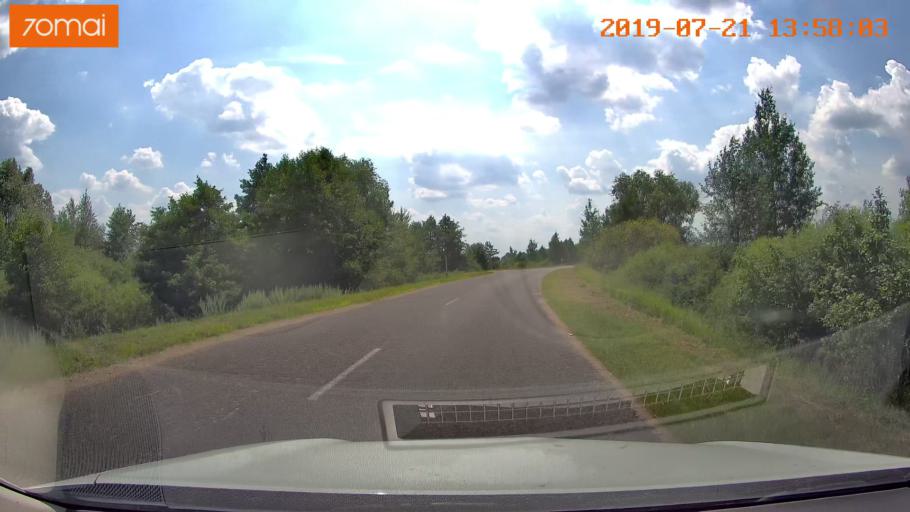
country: BY
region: Grodnenskaya
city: Lyubcha
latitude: 53.7647
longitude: 26.0859
